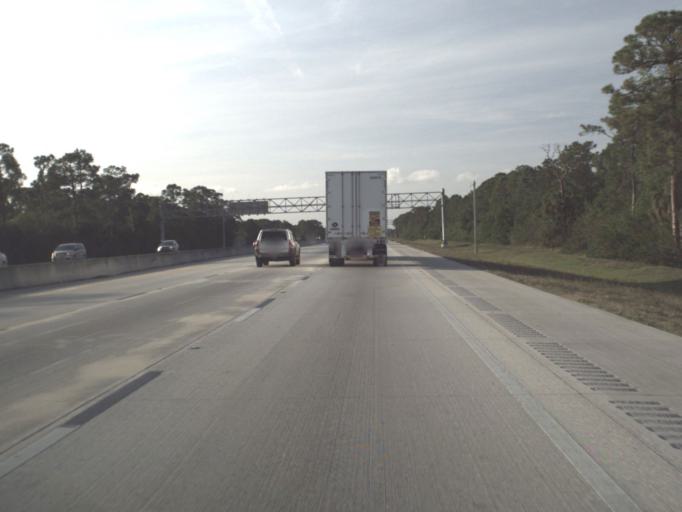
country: US
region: Florida
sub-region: Brevard County
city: Cocoa West
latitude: 28.3927
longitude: -80.8152
